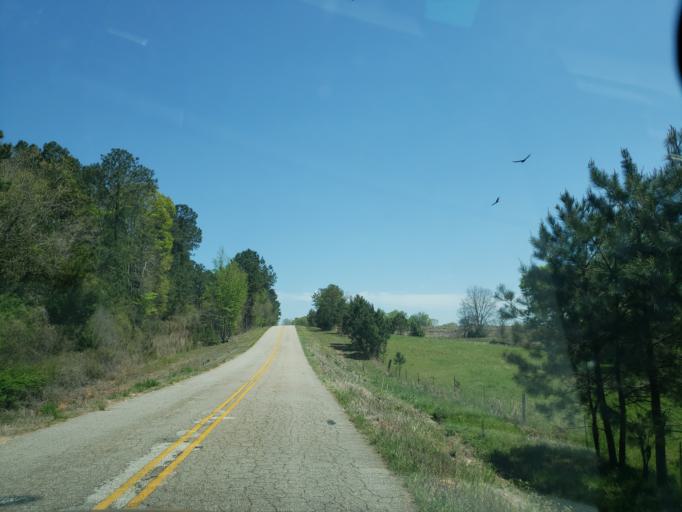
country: US
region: Alabama
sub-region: Tallapoosa County
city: Camp Hill
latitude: 32.6787
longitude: -85.6947
